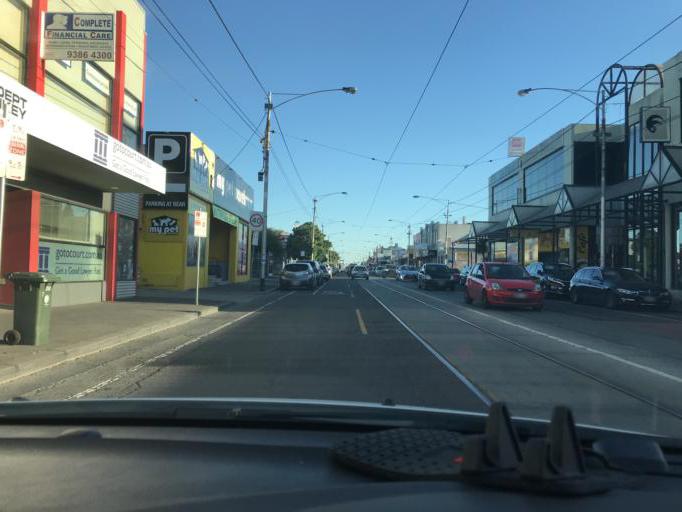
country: AU
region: Victoria
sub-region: Moreland
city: Coburg
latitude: -37.7487
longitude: 144.9653
